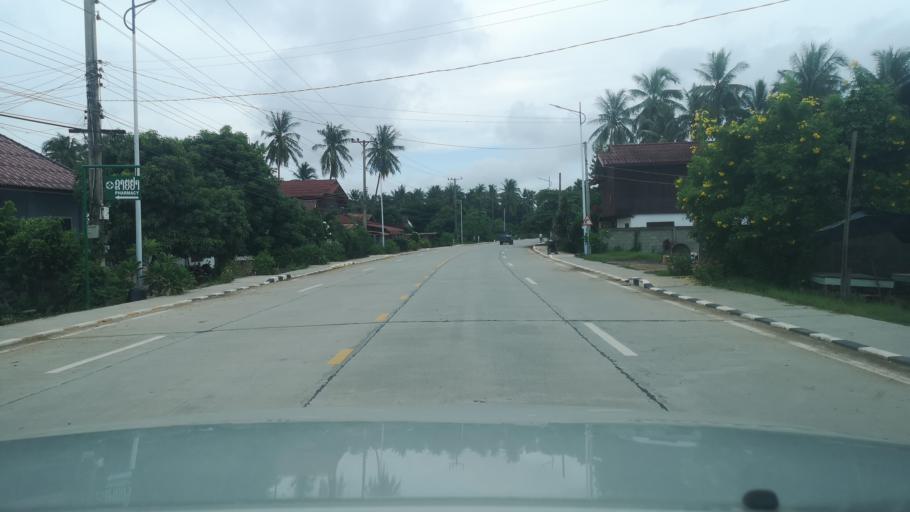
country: TH
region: Nong Khai
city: Tha Bo
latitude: 17.8259
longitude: 102.6569
